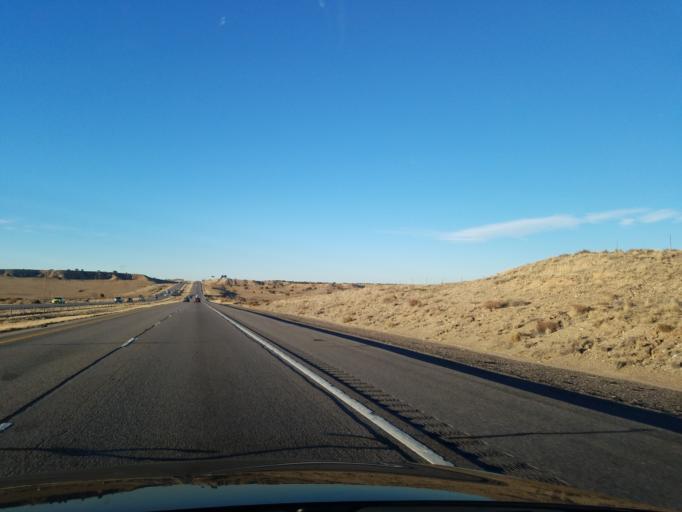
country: US
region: New Mexico
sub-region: Sandoval County
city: San Felipe Pueblo
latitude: 35.4379
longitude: -106.3743
